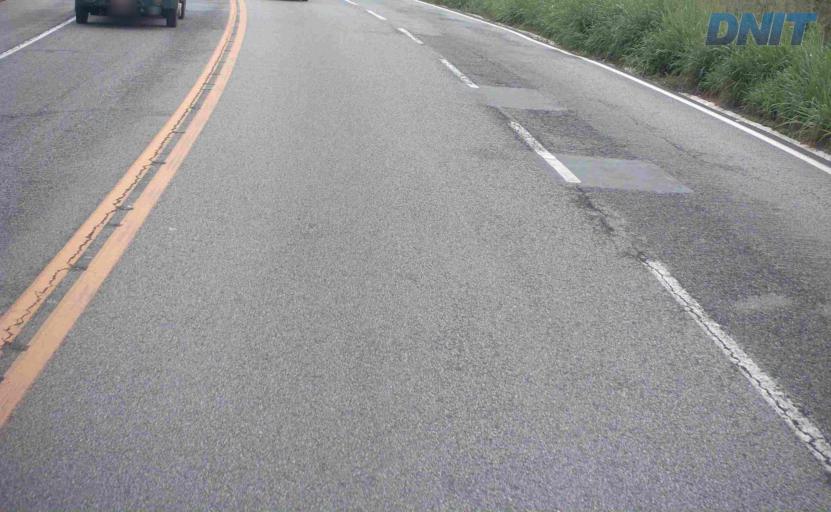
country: BR
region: Minas Gerais
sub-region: Barao De Cocais
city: Barao de Cocais
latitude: -19.8343
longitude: -43.3663
